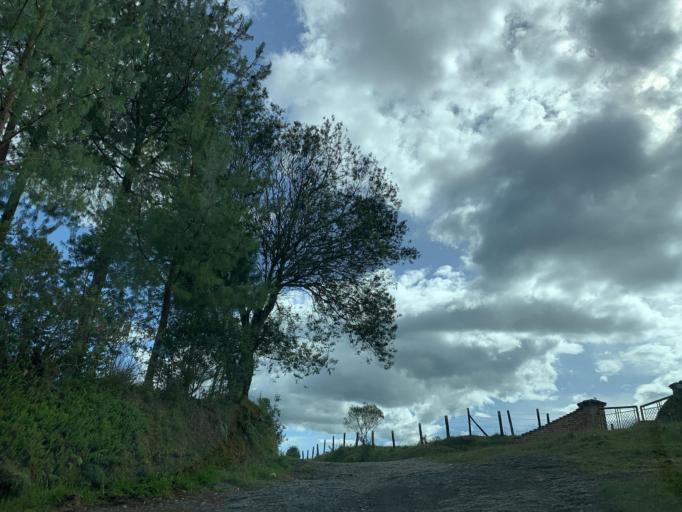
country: CO
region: Boyaca
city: Arcabuco
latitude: 5.7908
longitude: -73.4552
